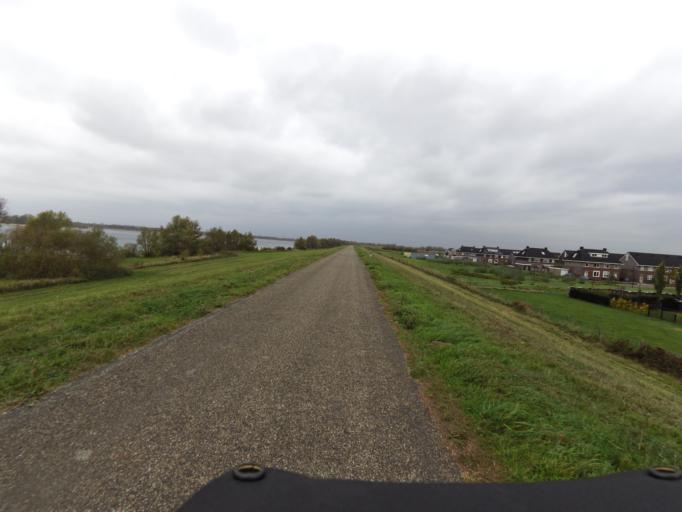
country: NL
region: Gelderland
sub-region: Gemeente Zevenaar
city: Zevenaar
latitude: 51.8604
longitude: 6.1001
